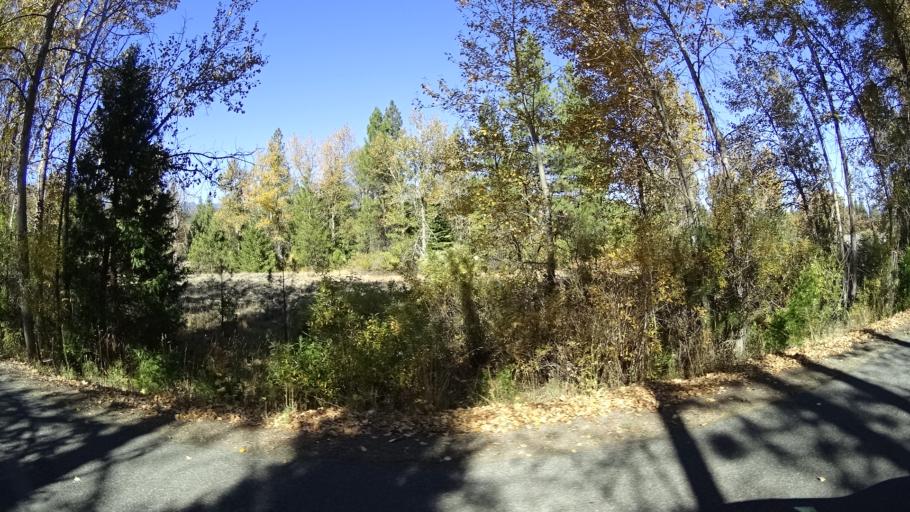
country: US
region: California
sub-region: Siskiyou County
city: Yreka
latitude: 41.5348
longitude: -122.9379
